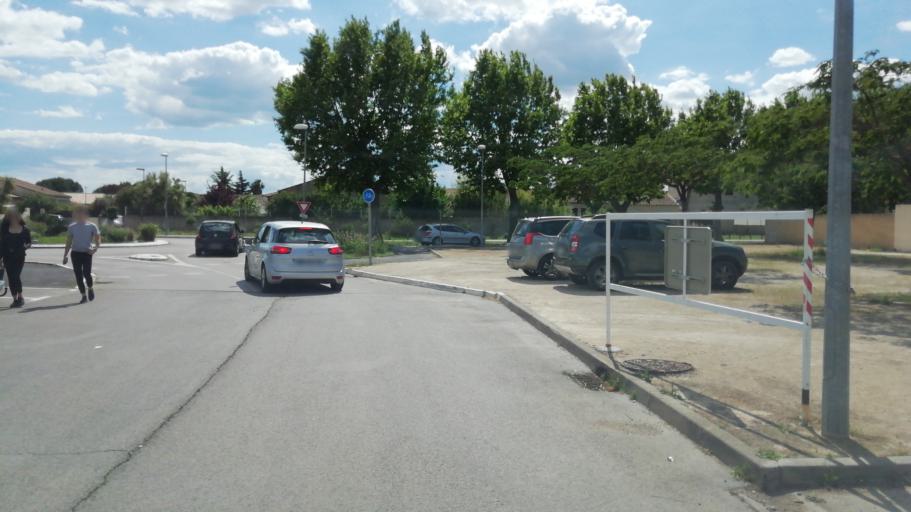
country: FR
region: Languedoc-Roussillon
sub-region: Departement de l'Herault
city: Saint-Just
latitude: 43.6581
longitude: 4.1174
